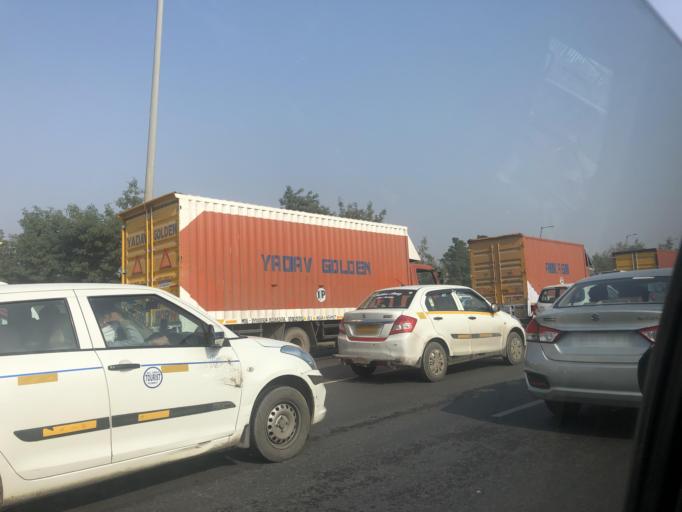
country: IN
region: Haryana
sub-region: Gurgaon
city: Gurgaon
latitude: 28.5349
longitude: 77.1103
